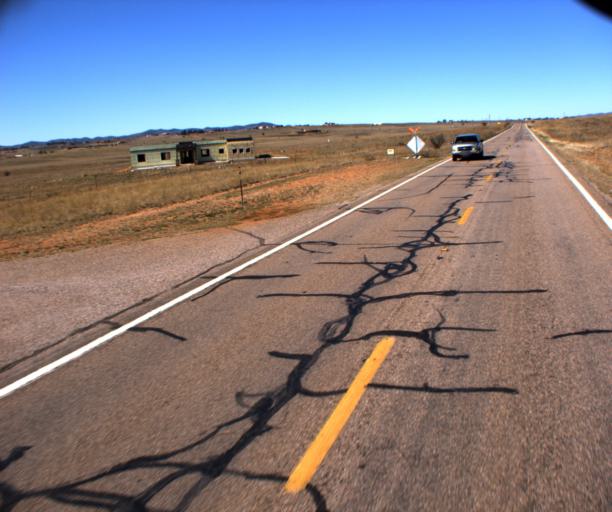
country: US
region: Arizona
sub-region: Cochise County
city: Huachuca City
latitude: 31.6883
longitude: -110.6152
